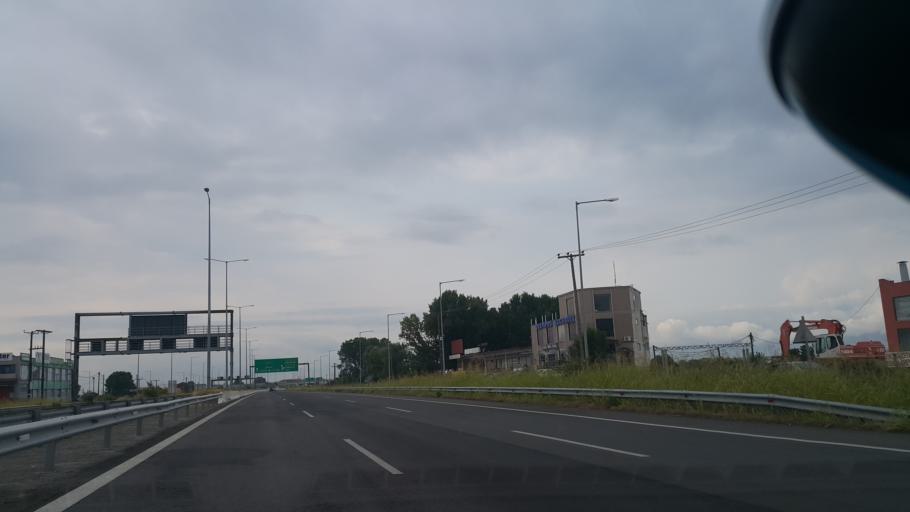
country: GR
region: Central Macedonia
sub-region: Nomos Pierias
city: Peristasi
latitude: 40.2631
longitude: 22.5280
